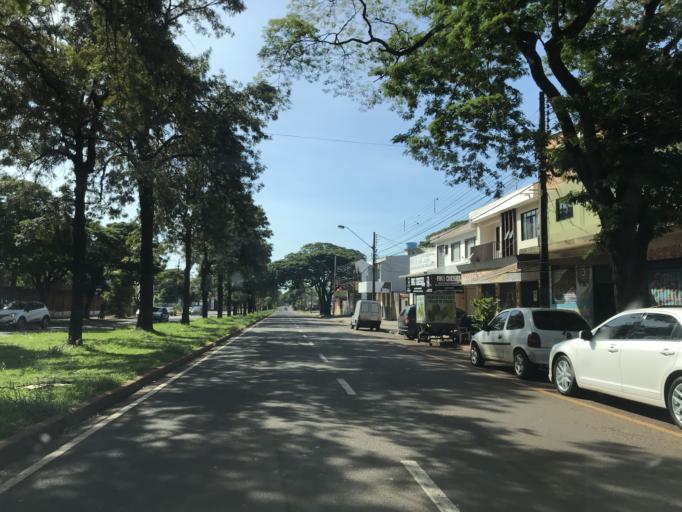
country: BR
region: Parana
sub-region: Maringa
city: Maringa
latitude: -23.3968
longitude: -51.9257
